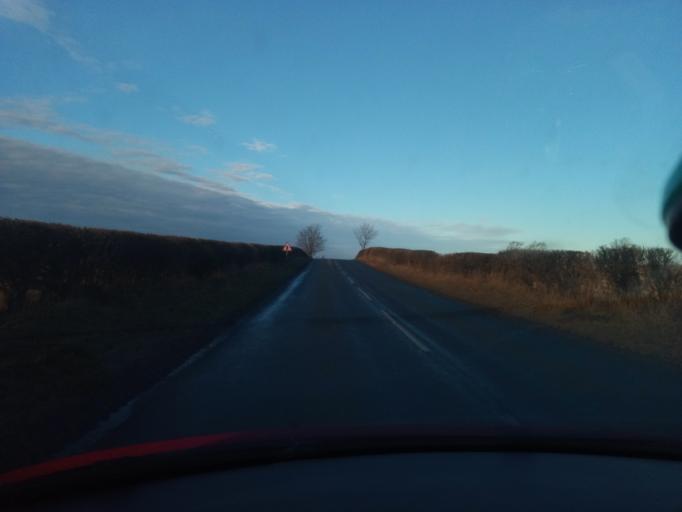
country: GB
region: England
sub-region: Darlington
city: High Coniscliffe
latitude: 54.4825
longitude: -1.6700
